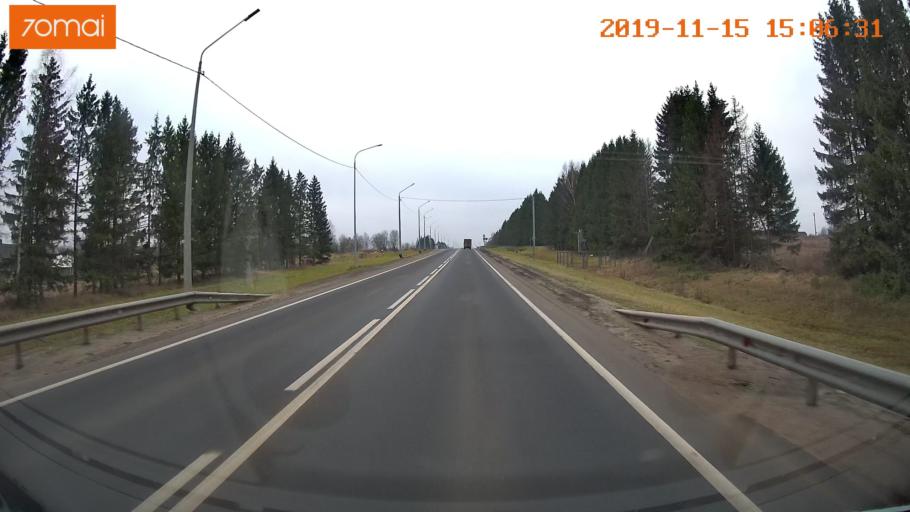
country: RU
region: Jaroslavl
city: Prechistoye
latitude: 58.3918
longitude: 40.3090
